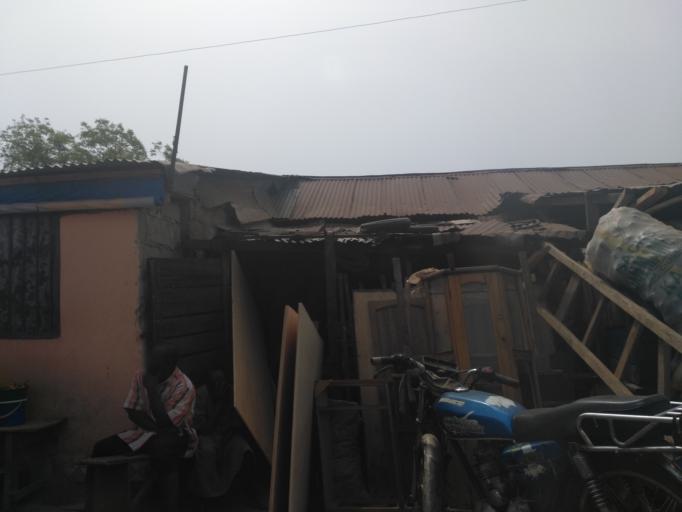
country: GH
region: Ashanti
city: Kumasi
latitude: 6.7020
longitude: -1.6106
